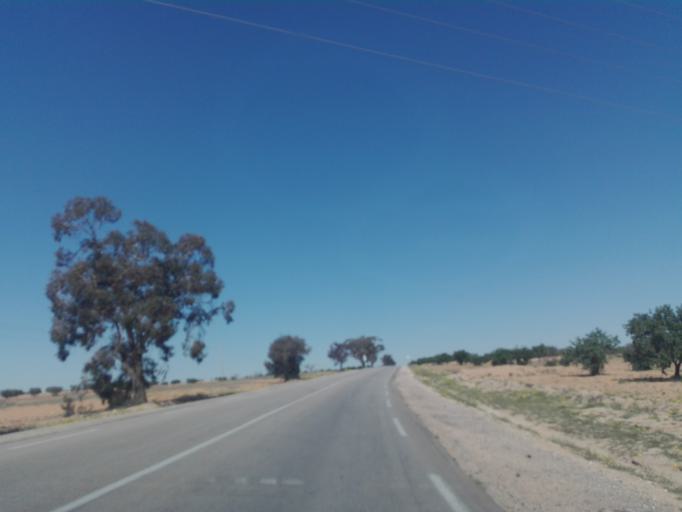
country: TN
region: Safaqis
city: Bi'r `Ali Bin Khalifah
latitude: 34.7470
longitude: 10.3554
